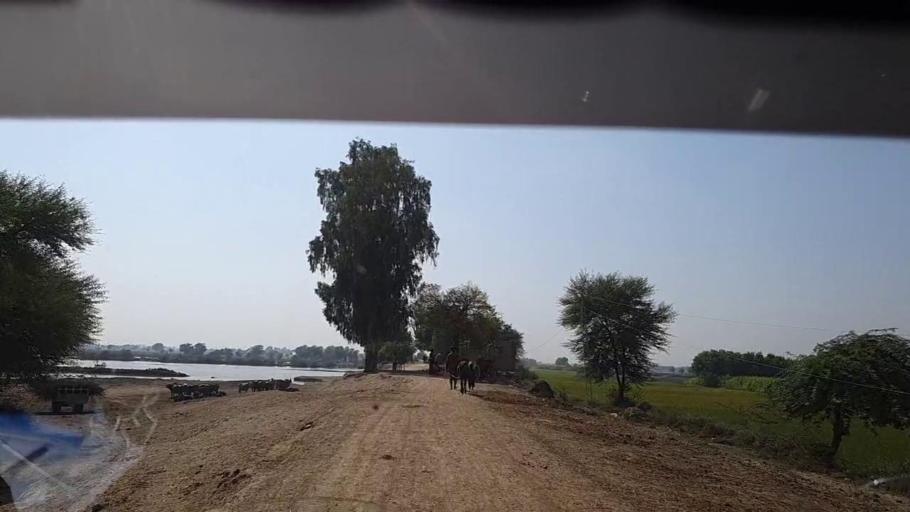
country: PK
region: Sindh
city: Naudero
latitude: 27.6606
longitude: 68.3798
